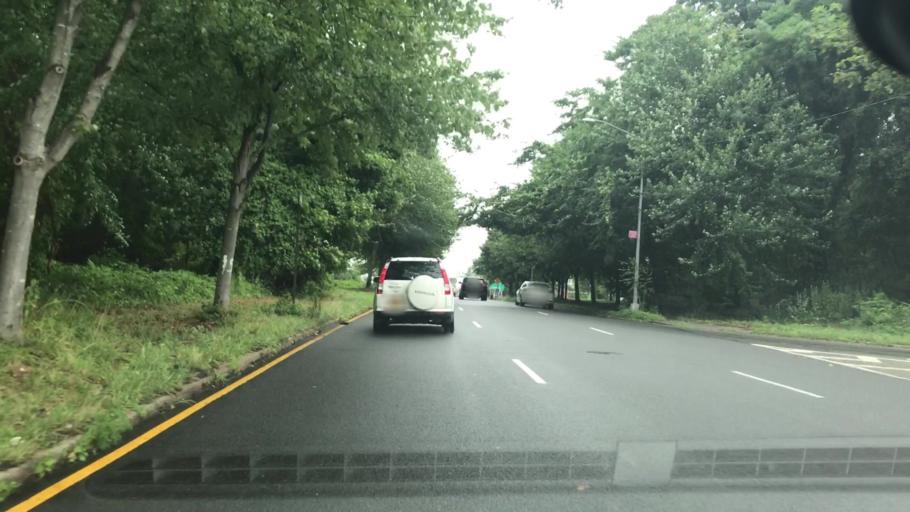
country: US
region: New Jersey
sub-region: Hudson County
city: Bayonne
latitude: 40.6039
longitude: -74.0770
